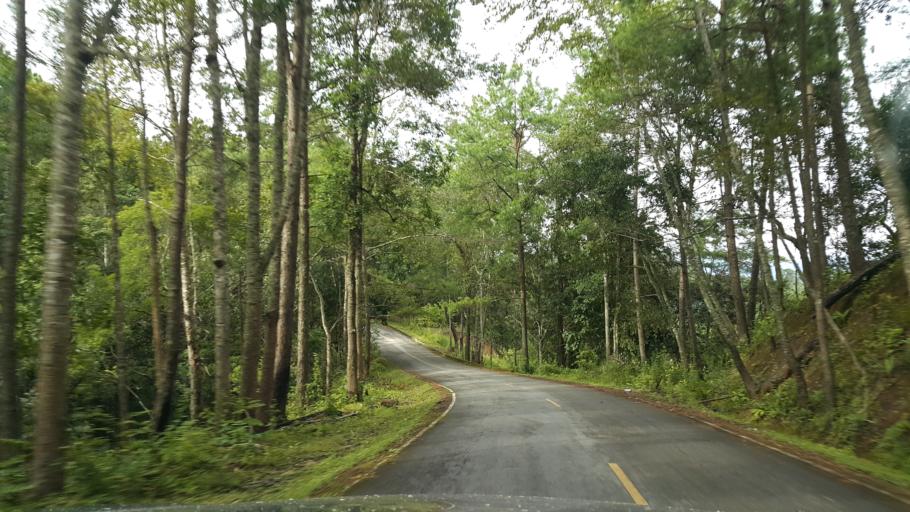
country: TH
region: Chiang Mai
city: Samoeng
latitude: 18.9077
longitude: 98.5060
